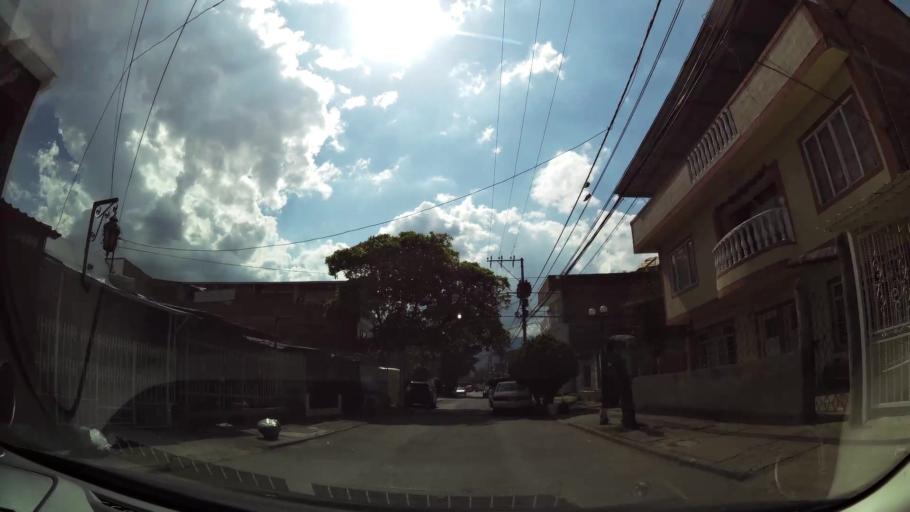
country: CO
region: Valle del Cauca
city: Cali
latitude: 3.4191
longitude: -76.5146
